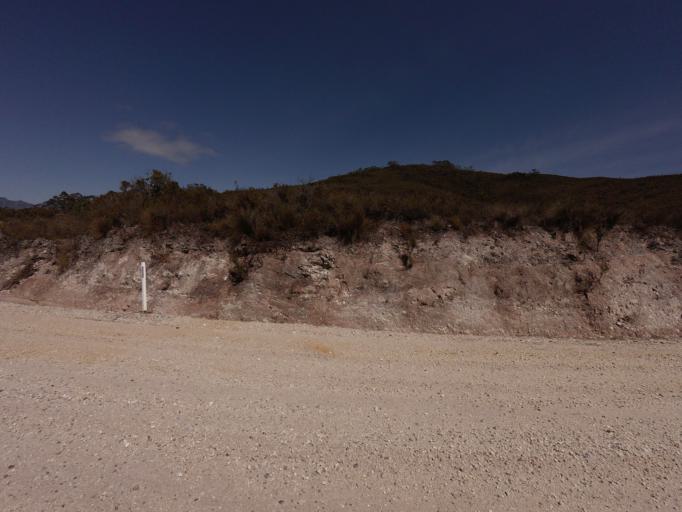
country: AU
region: Tasmania
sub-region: Huon Valley
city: Geeveston
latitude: -43.0334
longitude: 146.2929
